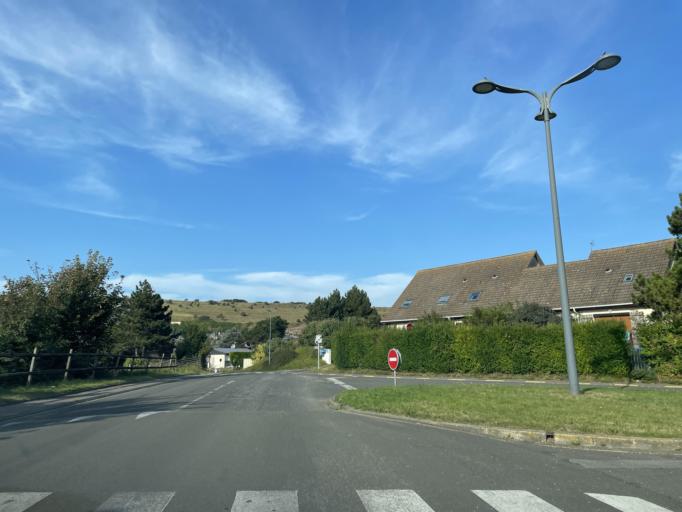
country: FR
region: Picardie
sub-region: Departement de la Somme
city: Mers-les-Bains
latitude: 50.0690
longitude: 1.3925
